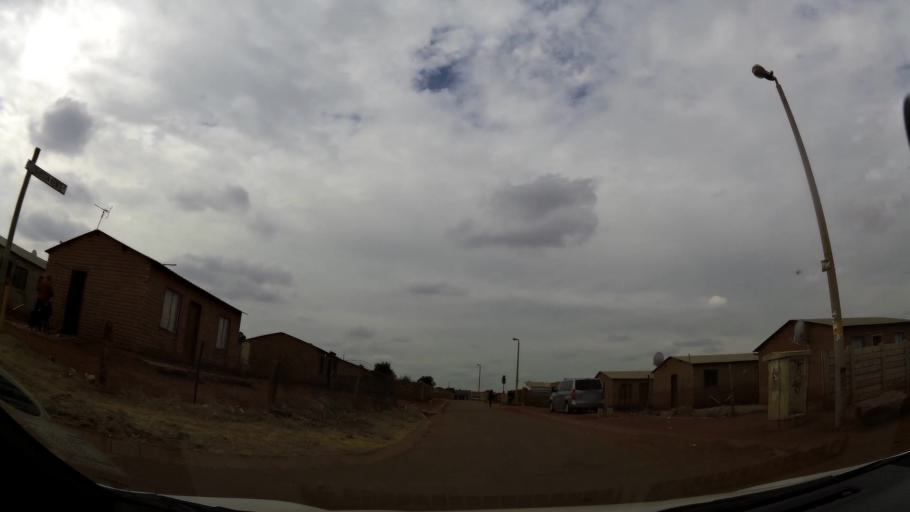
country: ZA
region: Gauteng
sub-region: Ekurhuleni Metropolitan Municipality
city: Germiston
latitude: -26.3865
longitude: 28.1213
